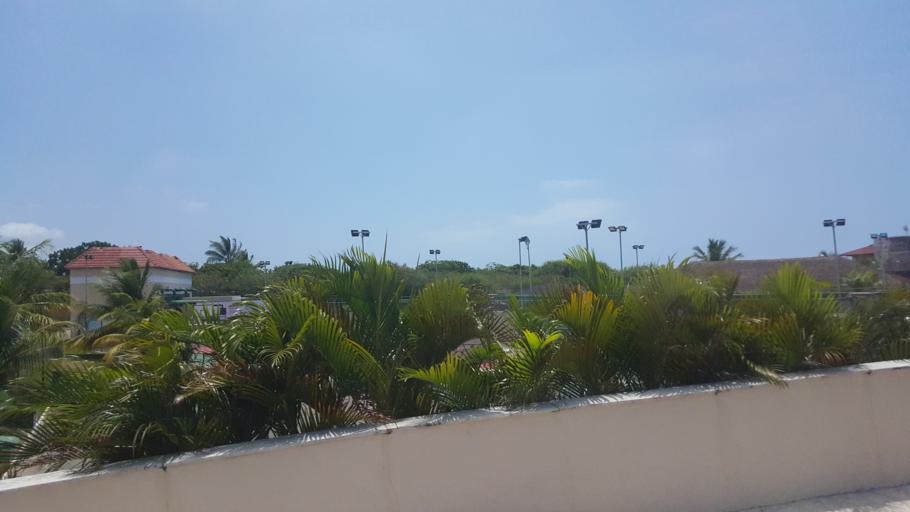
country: BR
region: Bahia
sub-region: Mata De Sao Joao
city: Mata de Sao Joao
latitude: -12.4818
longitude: -37.9561
